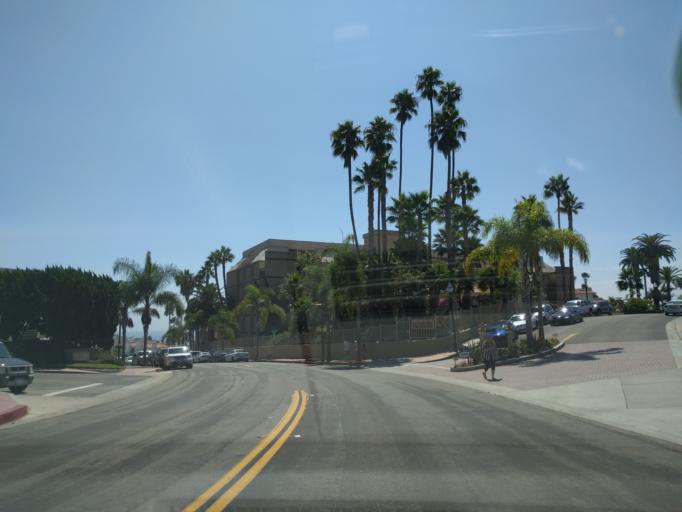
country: US
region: California
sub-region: Orange County
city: San Clemente
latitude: 33.4229
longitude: -117.6188
